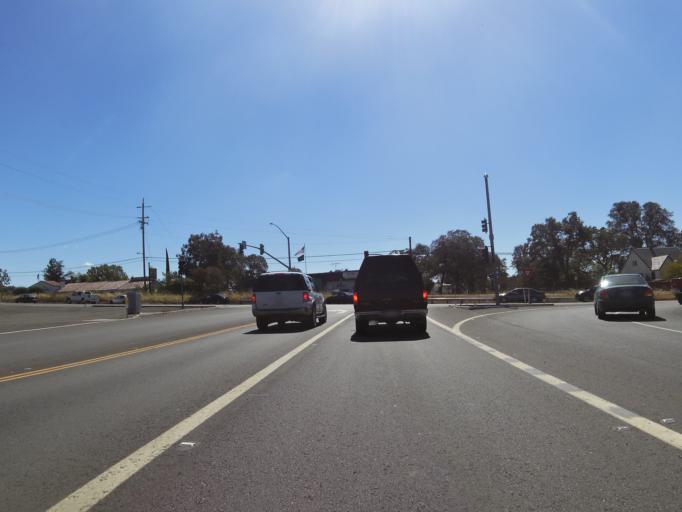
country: US
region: California
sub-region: Amador County
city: Jackson
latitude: 38.3658
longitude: -120.7949
